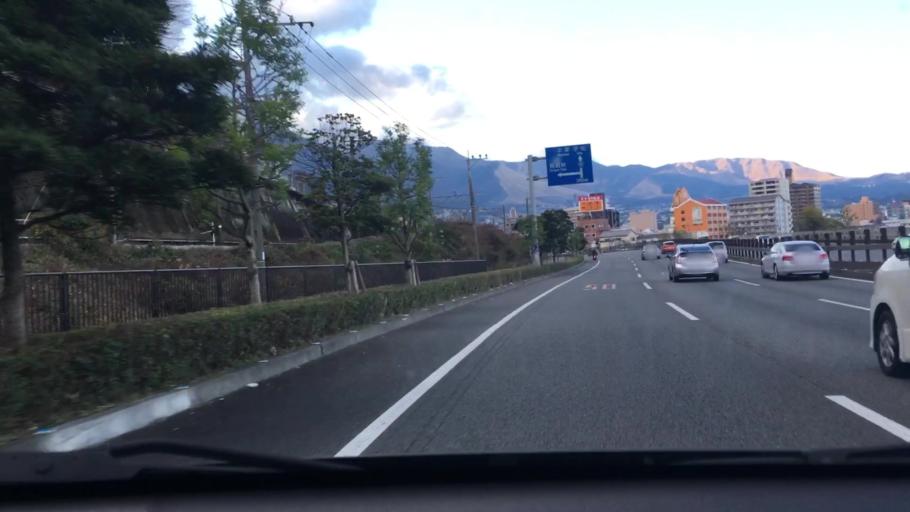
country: JP
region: Oita
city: Beppu
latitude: 33.2659
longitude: 131.5150
